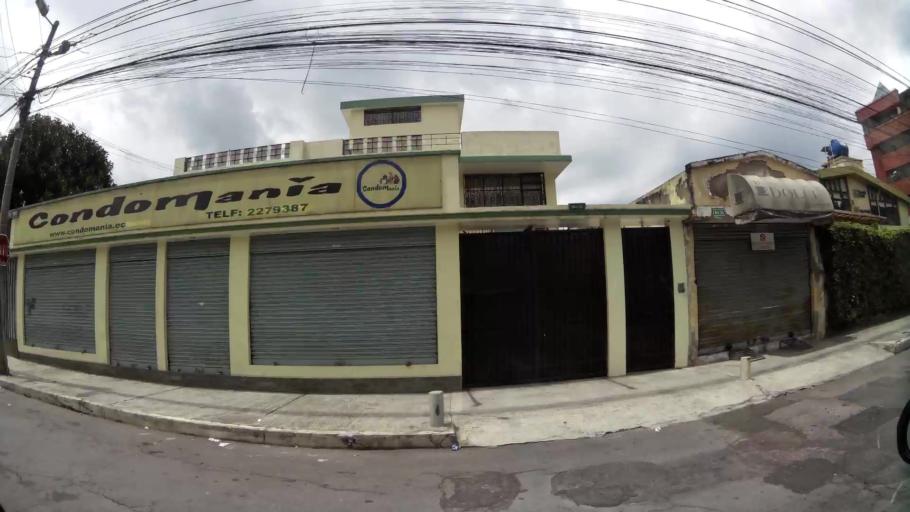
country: EC
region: Pichincha
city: Quito
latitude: -0.1655
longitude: -78.4782
